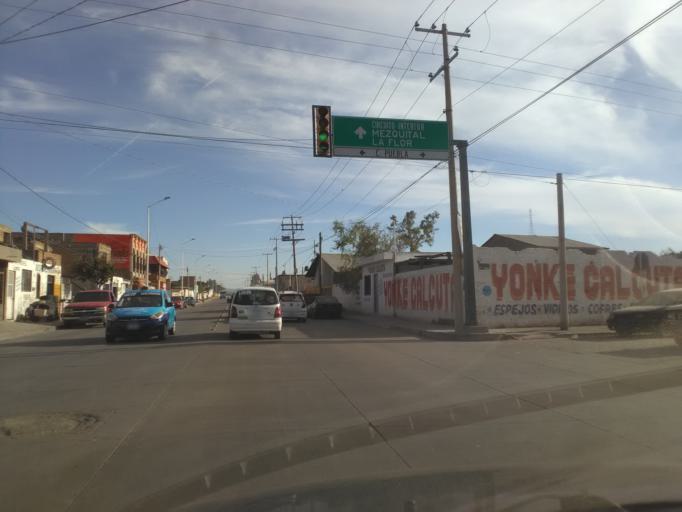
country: MX
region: Durango
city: Victoria de Durango
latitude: 24.0177
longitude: -104.6218
